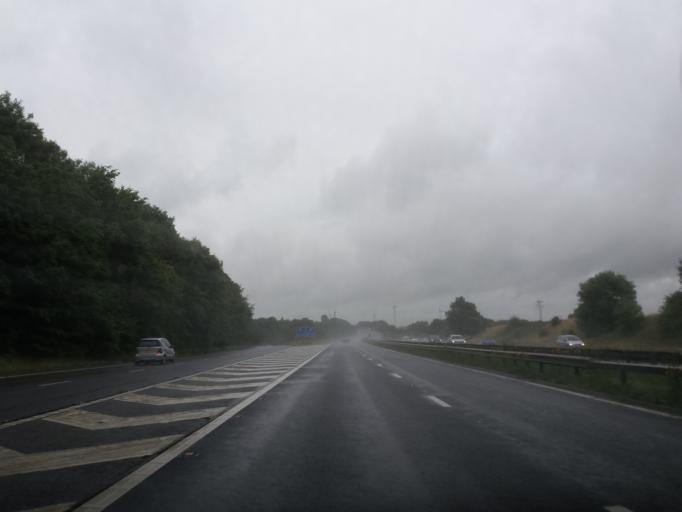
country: GB
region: England
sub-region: Rotherham
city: Bramley
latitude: 53.4005
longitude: -1.2651
